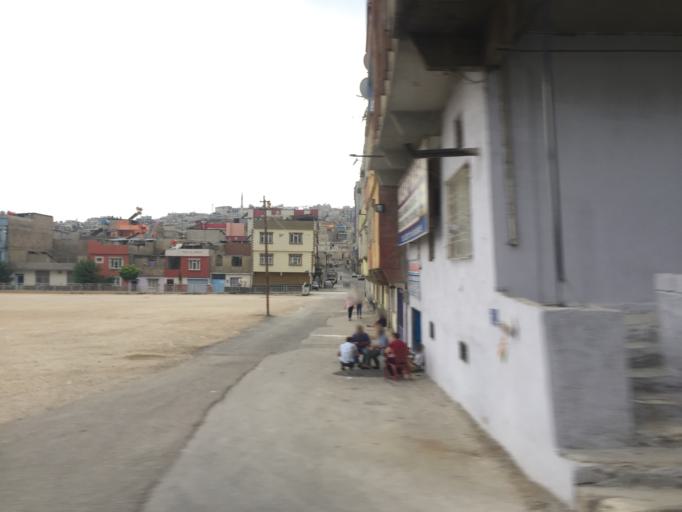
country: TR
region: Gaziantep
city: Gaziantep
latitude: 37.0708
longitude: 37.4135
